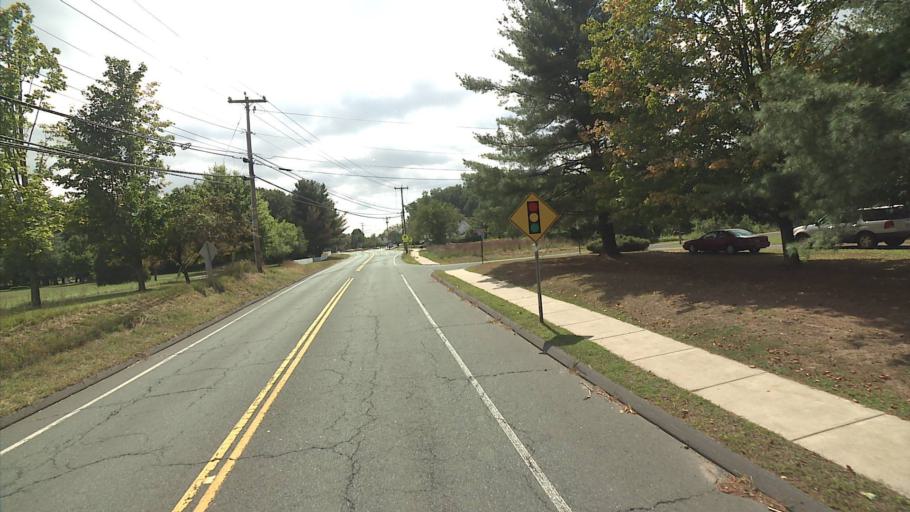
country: US
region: Connecticut
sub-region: Hartford County
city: Salmon Brook
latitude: 41.9581
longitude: -72.7949
